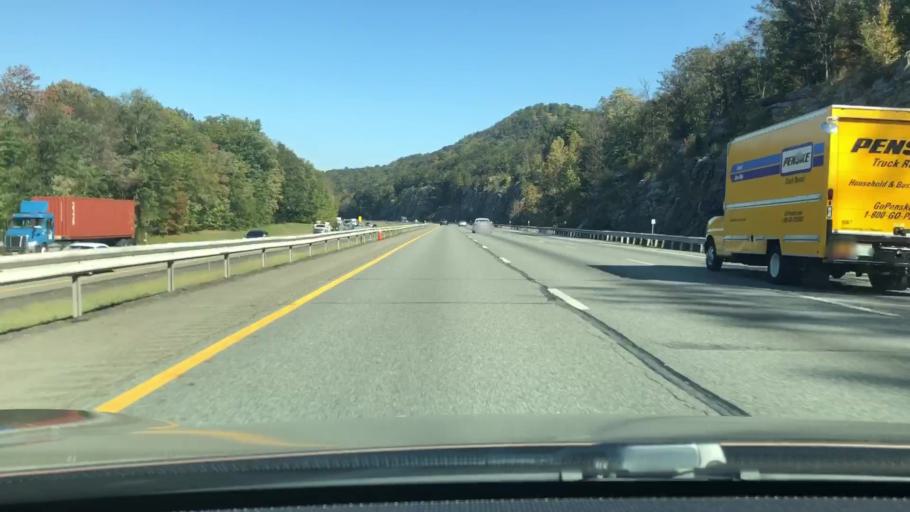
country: US
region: New York
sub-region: Rockland County
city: Sloatsburg
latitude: 41.1810
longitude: -74.1825
